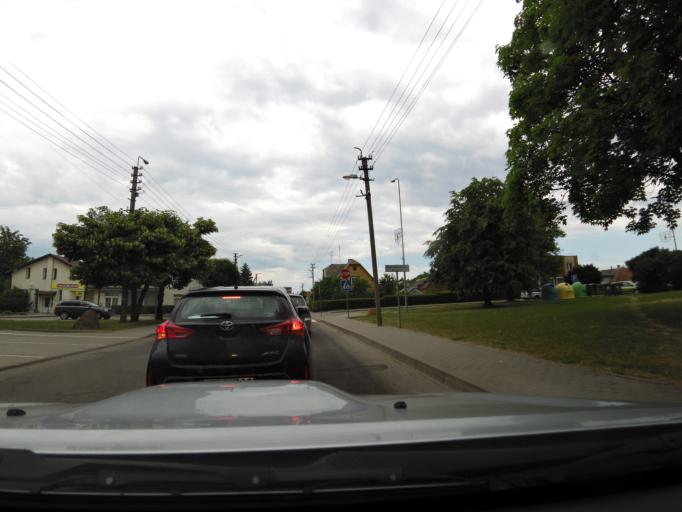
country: LT
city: Vilkaviskis
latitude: 54.6511
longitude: 23.0338
